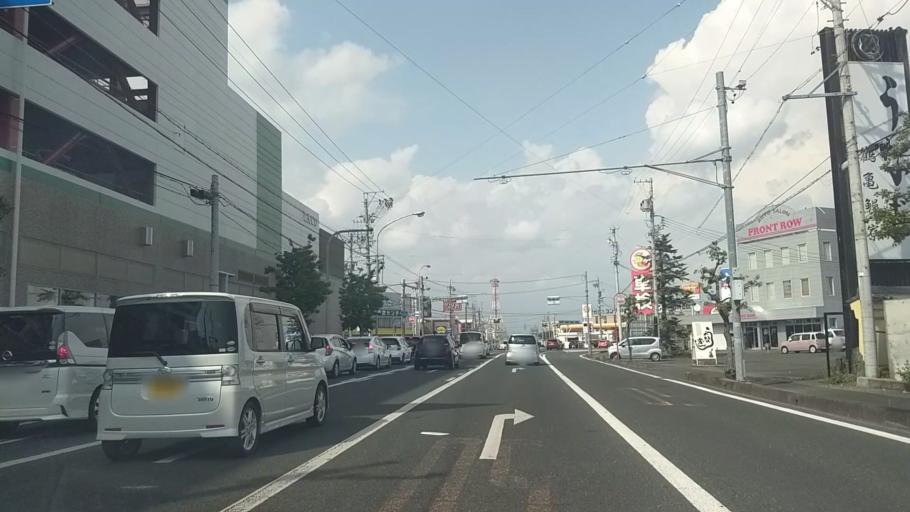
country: JP
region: Shizuoka
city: Hamamatsu
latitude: 34.7199
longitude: 137.7642
